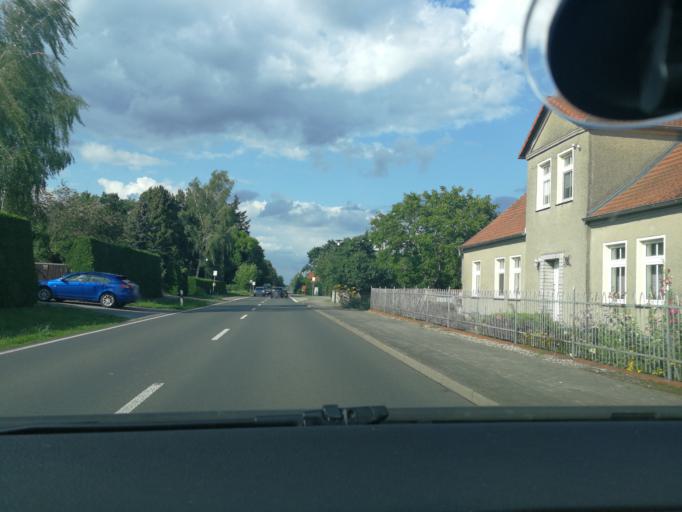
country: DE
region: Brandenburg
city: Pritzwalk
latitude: 53.1919
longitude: 12.1972
